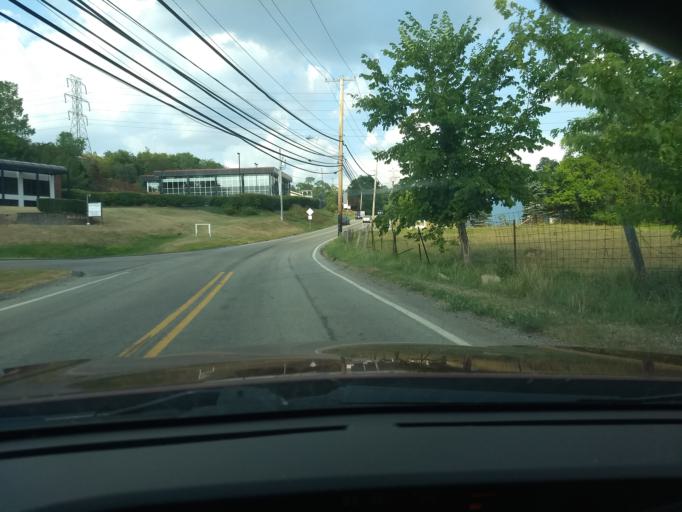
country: US
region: Pennsylvania
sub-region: Allegheny County
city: Plum
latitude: 40.4772
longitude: -79.7442
